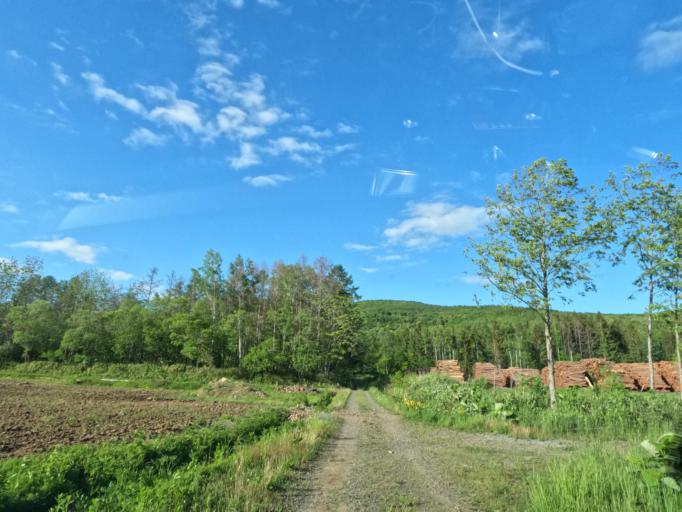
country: JP
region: Hokkaido
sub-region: Asahikawa-shi
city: Asahikawa
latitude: 43.9216
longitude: 142.4961
